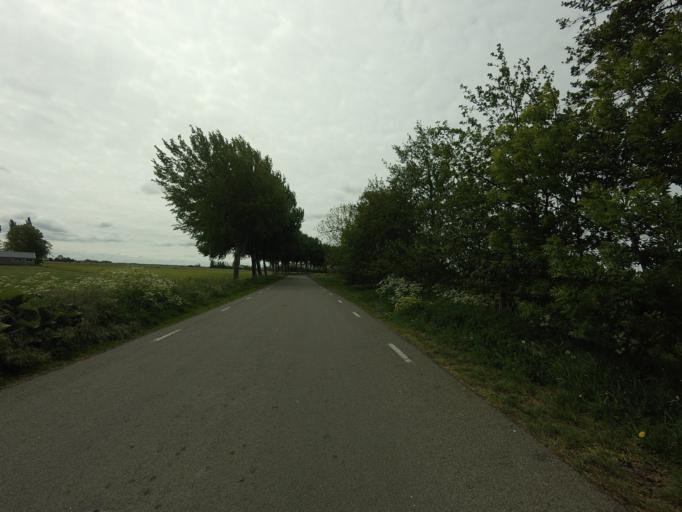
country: NL
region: Friesland
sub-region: Sudwest Fryslan
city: Workum
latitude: 52.9497
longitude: 5.4988
